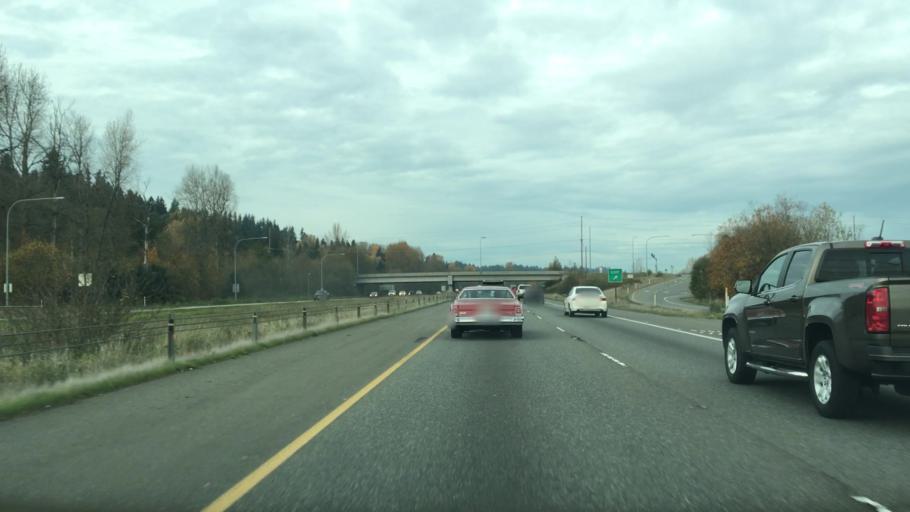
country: US
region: Washington
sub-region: Pierce County
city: Sumner
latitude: 47.2330
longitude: -122.2505
